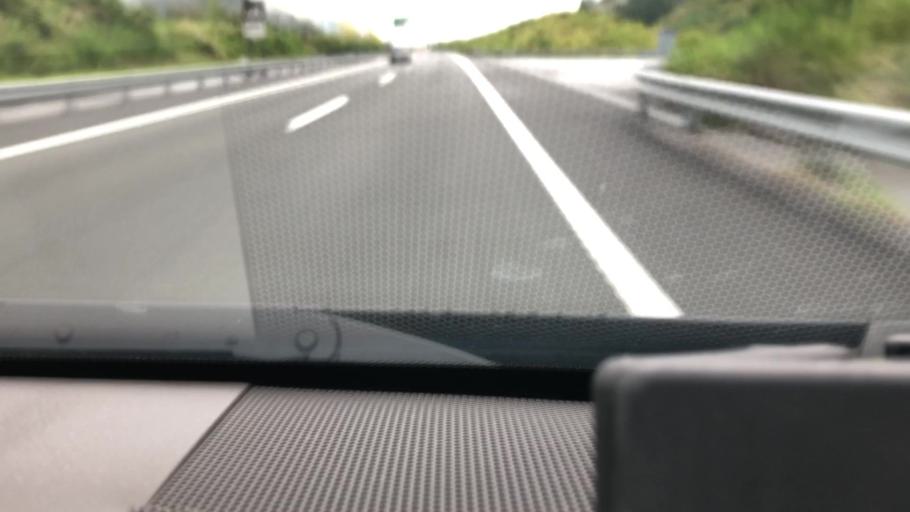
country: JP
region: Shizuoka
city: Shizuoka-shi
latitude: 34.9642
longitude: 138.2901
